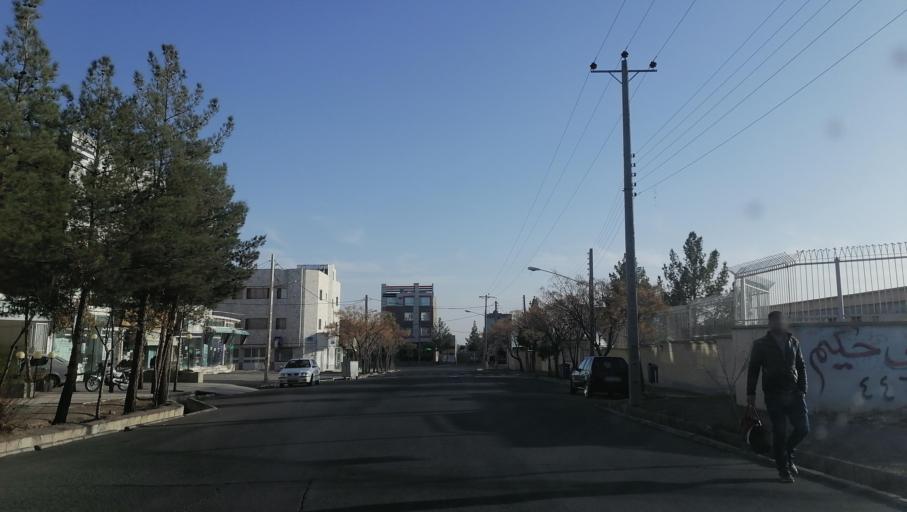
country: IR
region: Razavi Khorasan
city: Sabzevar
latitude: 36.2866
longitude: 57.6767
